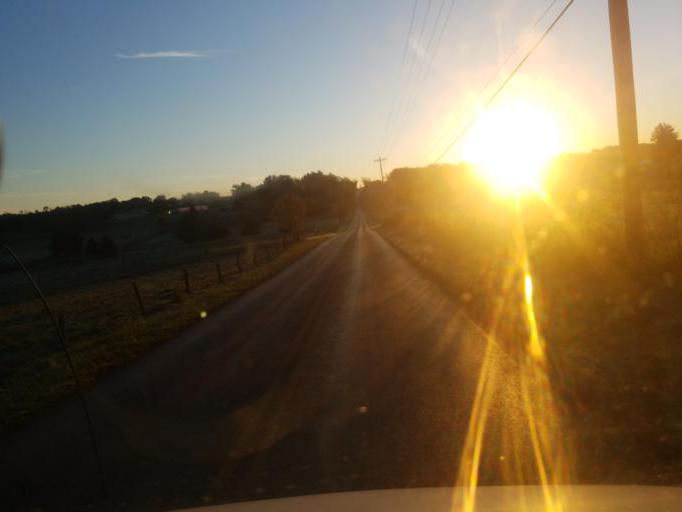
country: US
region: Ohio
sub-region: Stark County
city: Brewster
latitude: 40.6534
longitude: -81.7066
